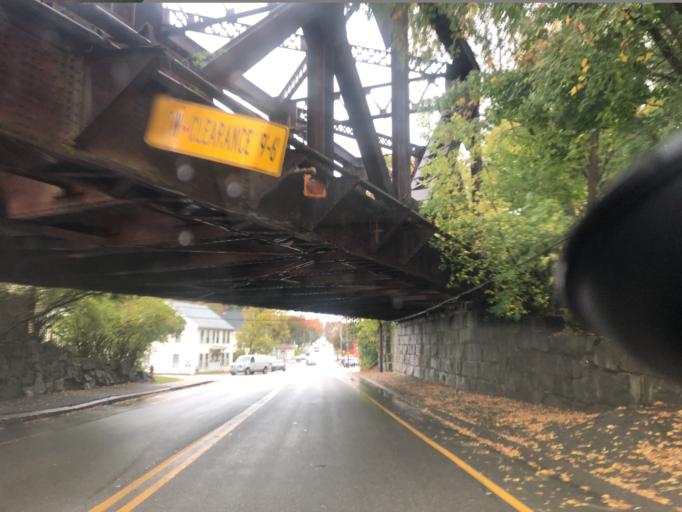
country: US
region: New Hampshire
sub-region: Strafford County
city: Dover
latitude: 43.1998
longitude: -70.8728
